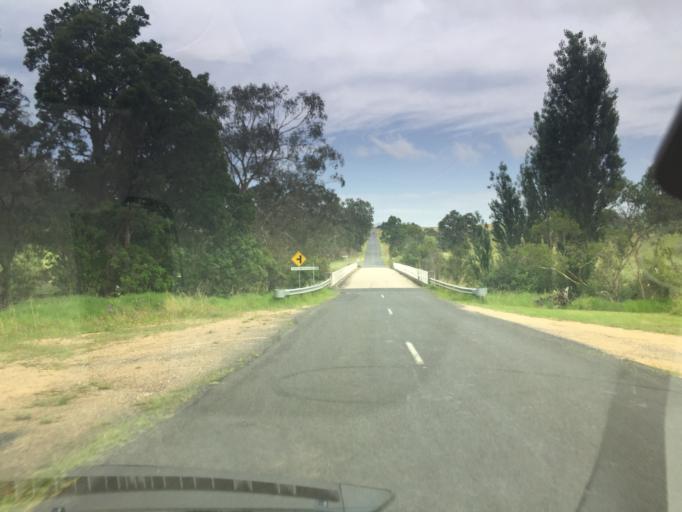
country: AU
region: New South Wales
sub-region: Bega Valley
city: Bega
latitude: -36.7408
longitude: 149.6490
